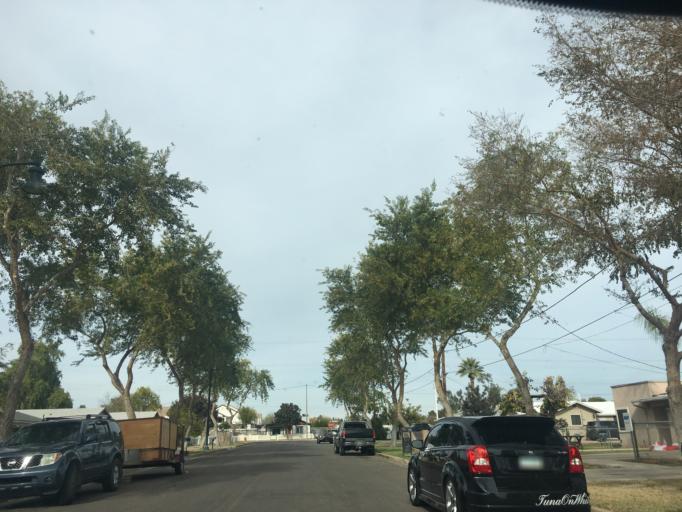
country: US
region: Arizona
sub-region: Maricopa County
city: Gilbert
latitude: 33.3551
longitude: -111.7868
